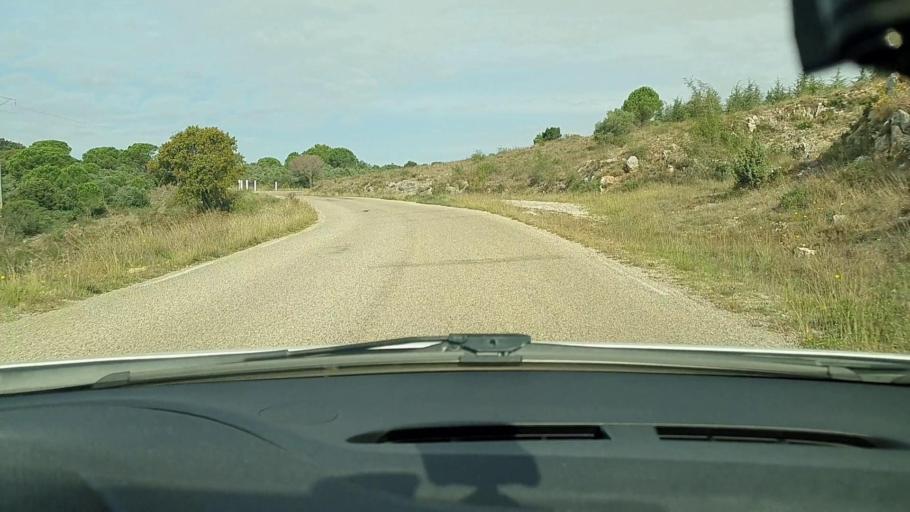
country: FR
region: Languedoc-Roussillon
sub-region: Departement du Gard
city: Saint-Quentin-la-Poterie
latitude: 44.1172
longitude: 4.4128
